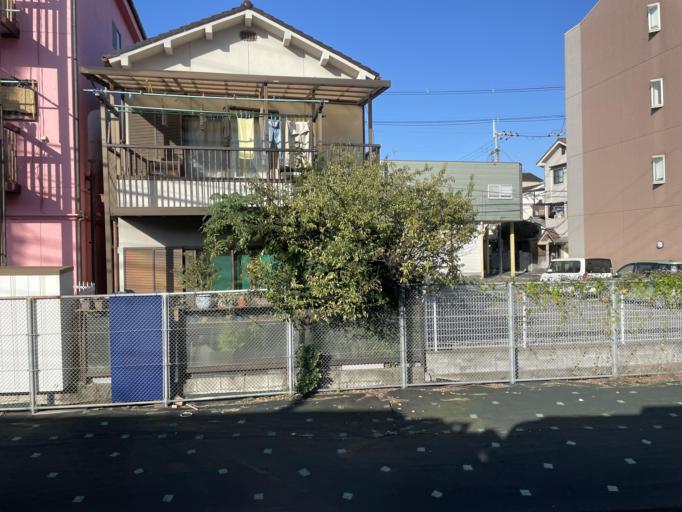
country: JP
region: Osaka
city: Kashihara
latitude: 34.5834
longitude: 135.6280
